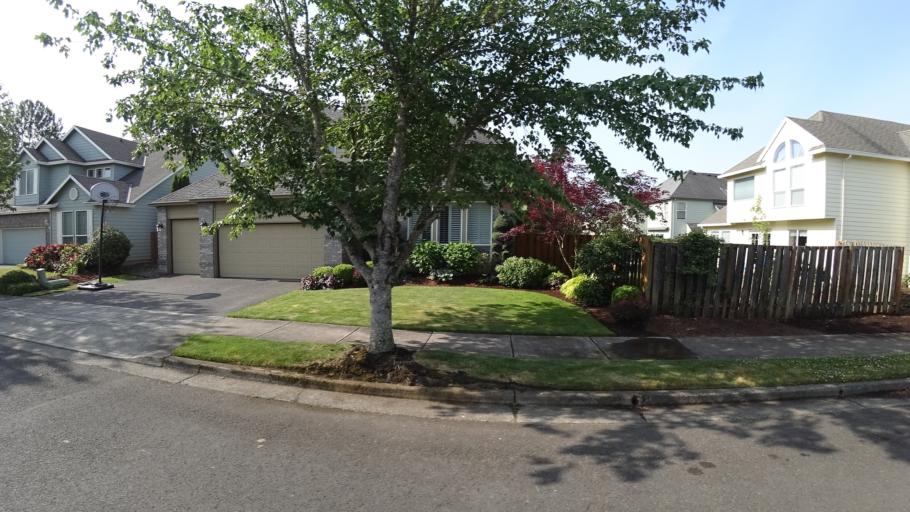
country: US
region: Oregon
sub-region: Clackamas County
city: Happy Valley
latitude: 45.4531
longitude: -122.5162
